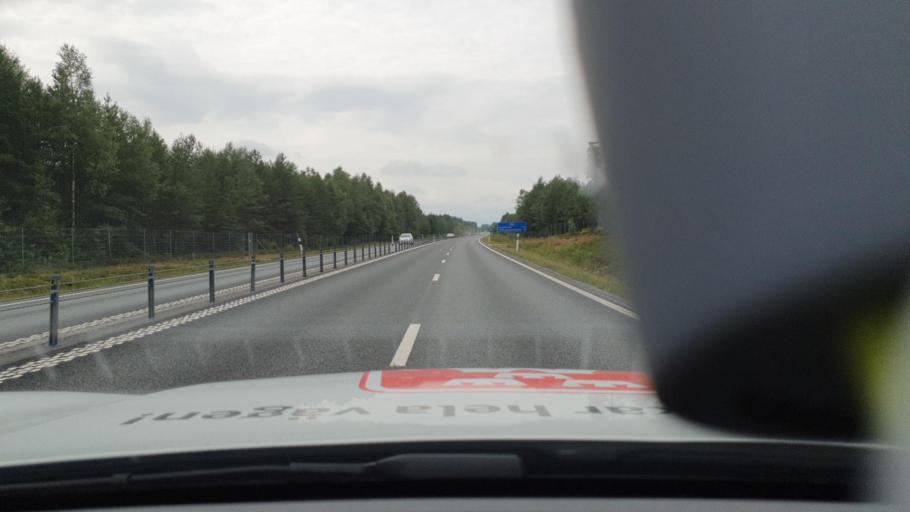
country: SE
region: Joenkoeping
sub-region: Gislaveds Kommun
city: Gislaved
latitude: 57.3199
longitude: 13.5402
